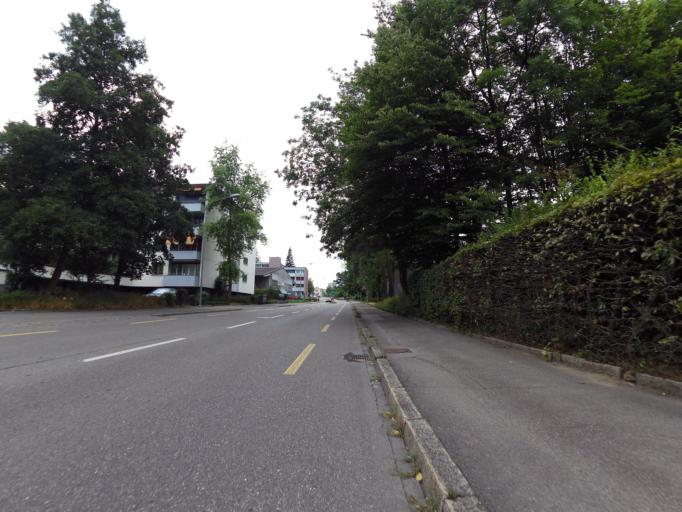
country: CH
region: Zurich
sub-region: Bezirk Zuerich
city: Zuerich (Kreis 11)
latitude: 47.4137
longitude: 8.5226
